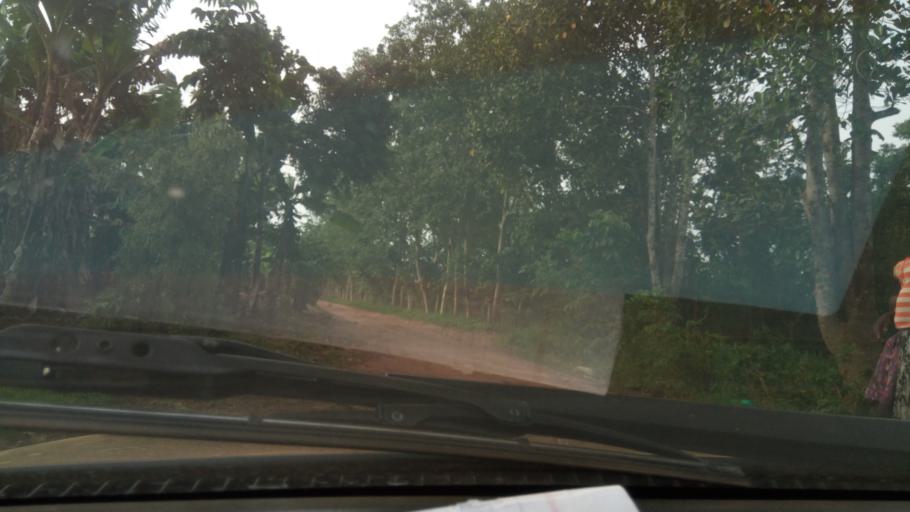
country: UG
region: Central Region
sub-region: Mityana District
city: Mityana
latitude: 0.5598
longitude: 32.1968
